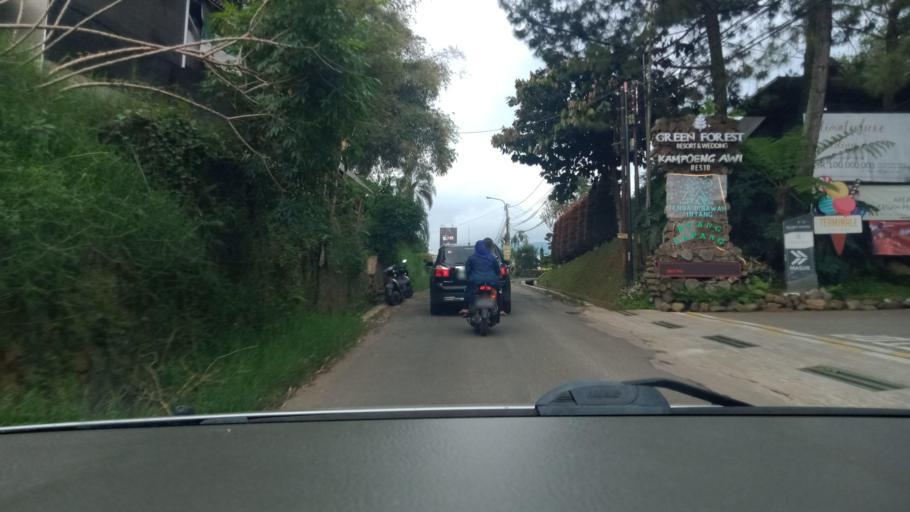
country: ID
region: West Java
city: Lembang
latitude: -6.8227
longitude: 107.5972
